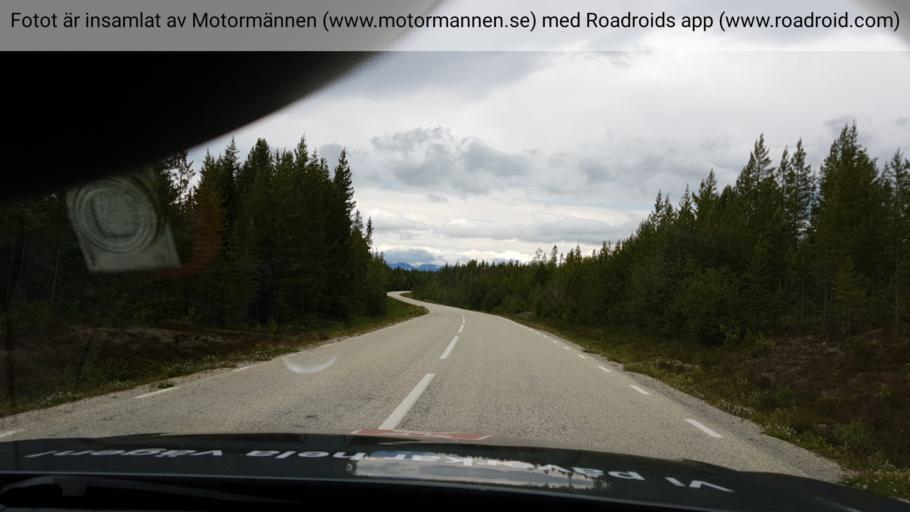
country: SE
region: Jaemtland
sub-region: Are Kommun
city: Jarpen
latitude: 62.8151
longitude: 13.5181
